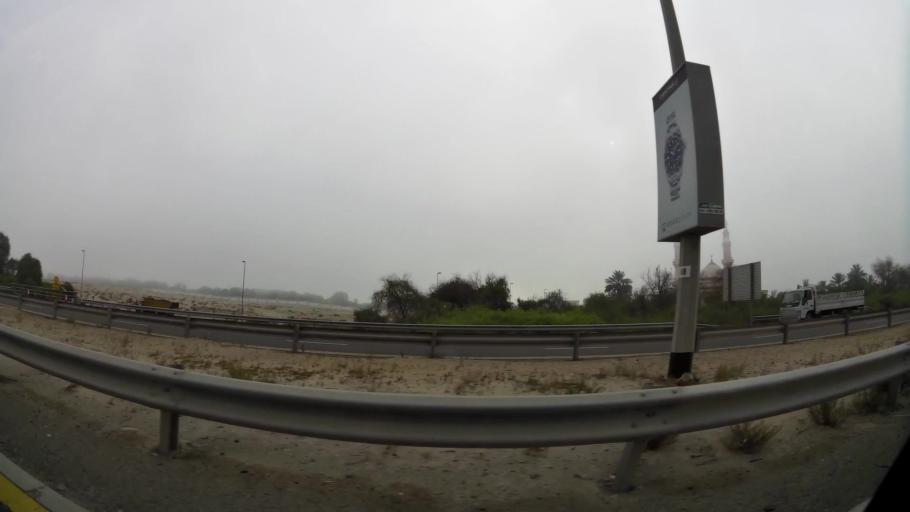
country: AE
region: Dubai
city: Dubai
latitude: 25.1597
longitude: 55.3325
